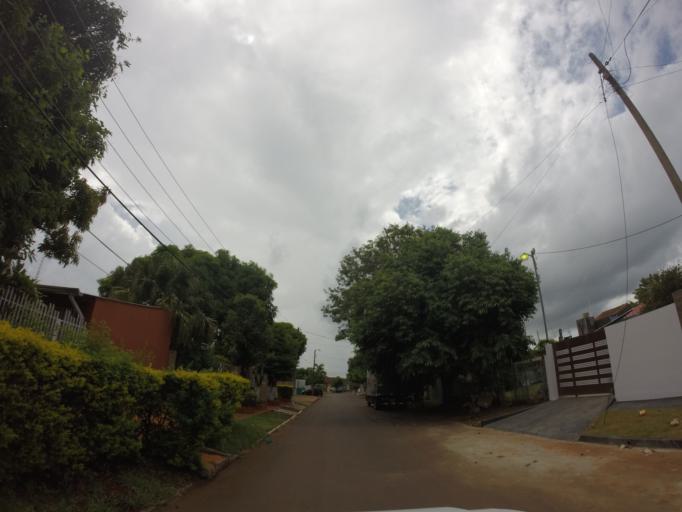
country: PY
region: Alto Parana
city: Ciudad del Este
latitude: -25.4152
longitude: -54.6278
